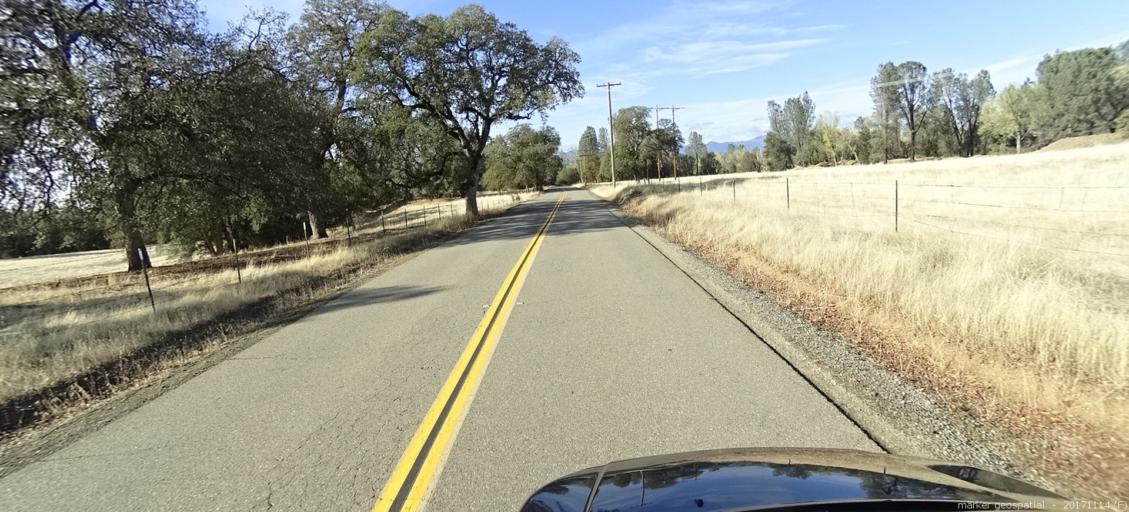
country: US
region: California
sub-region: Shasta County
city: Shasta
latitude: 40.3927
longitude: -122.5085
